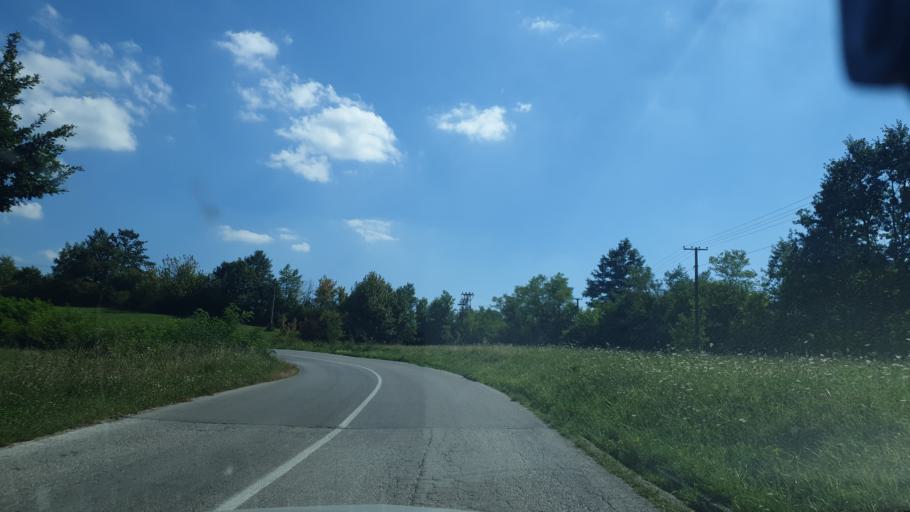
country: RS
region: Central Serbia
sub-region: Zlatiborski Okrug
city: Kosjeric
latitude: 44.0233
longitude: 20.0213
